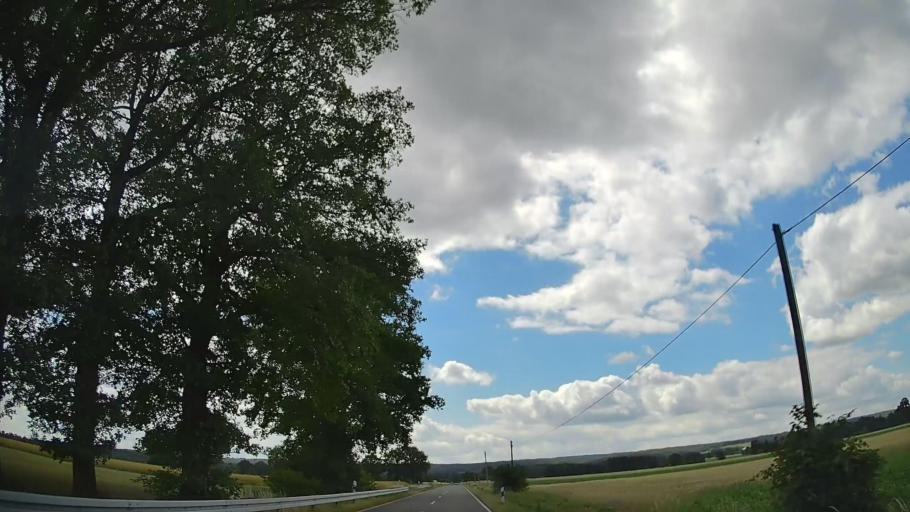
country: DE
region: Lower Saxony
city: Brockum
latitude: 52.4844
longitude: 8.4288
